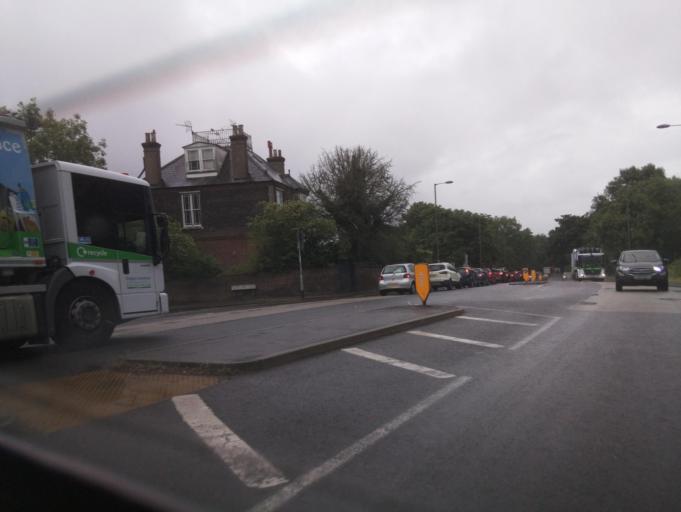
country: GB
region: England
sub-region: Surrey
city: Redhill
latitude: 51.2281
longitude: -0.1743
